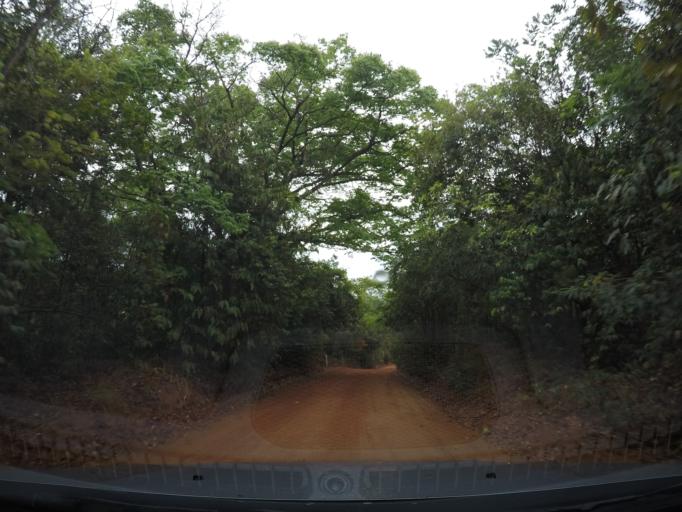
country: BR
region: Goias
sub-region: Pirenopolis
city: Pirenopolis
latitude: -15.8422
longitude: -48.9155
